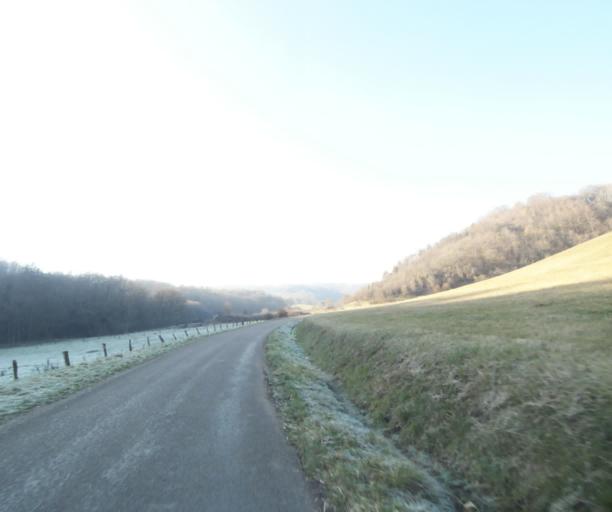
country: FR
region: Champagne-Ardenne
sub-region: Departement de la Haute-Marne
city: Joinville
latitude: 48.4891
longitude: 5.2051
